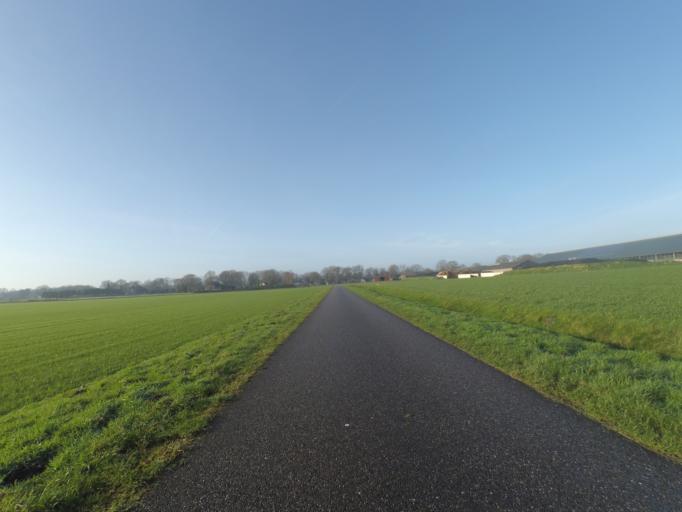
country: NL
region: Drenthe
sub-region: Gemeente Assen
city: Assen
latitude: 52.8806
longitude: 6.6521
